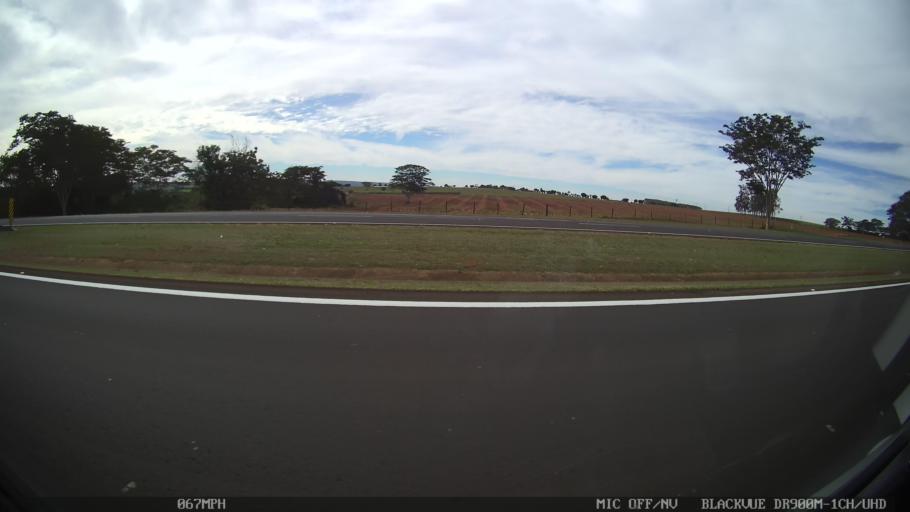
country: BR
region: Sao Paulo
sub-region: Taquaritinga
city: Taquaritinga
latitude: -21.4666
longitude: -48.6117
